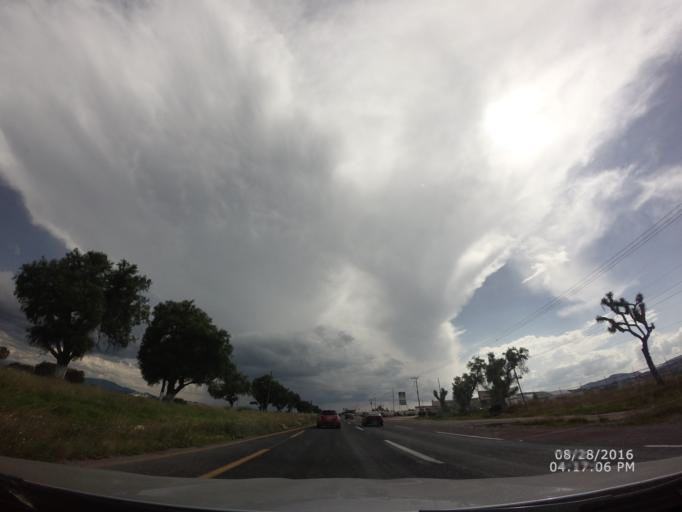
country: MX
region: Hidalgo
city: Zapotlan de Juarez
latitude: 19.9801
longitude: -98.8483
